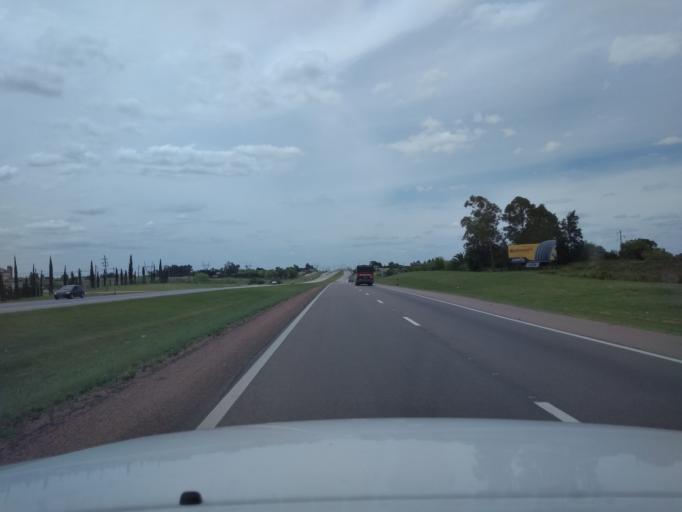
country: UY
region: Canelones
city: Las Piedras
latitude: -34.7319
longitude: -56.2490
